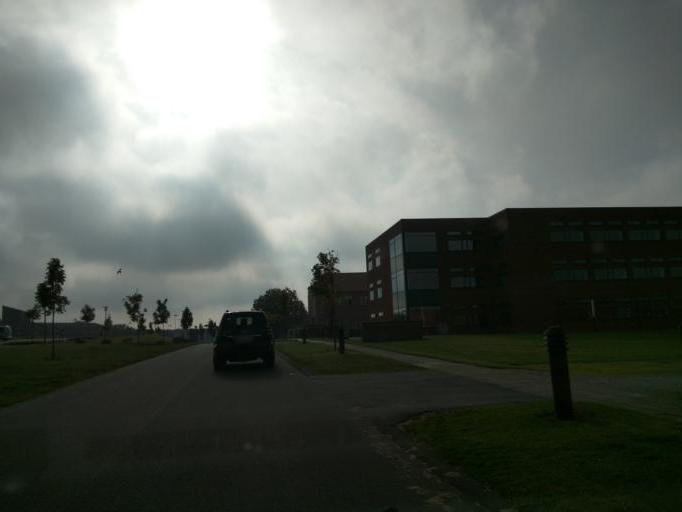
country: DK
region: Central Jutland
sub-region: Viborg Kommune
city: Viborg
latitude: 56.4507
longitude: 9.4312
